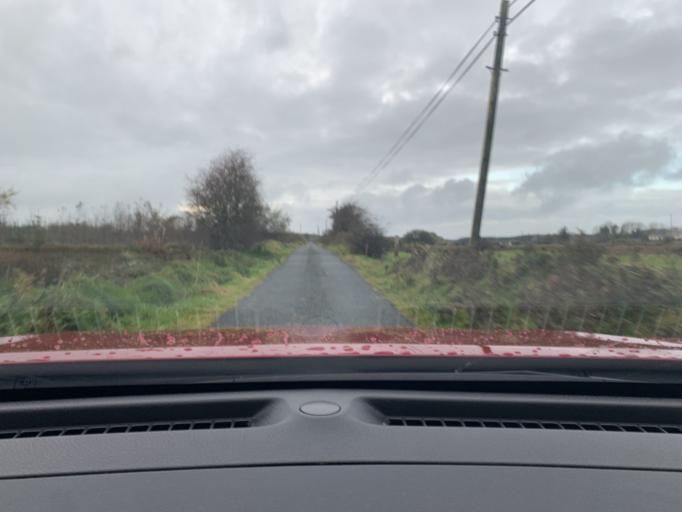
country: IE
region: Connaught
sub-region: Roscommon
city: Ballaghaderreen
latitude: 53.9677
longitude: -8.5827
